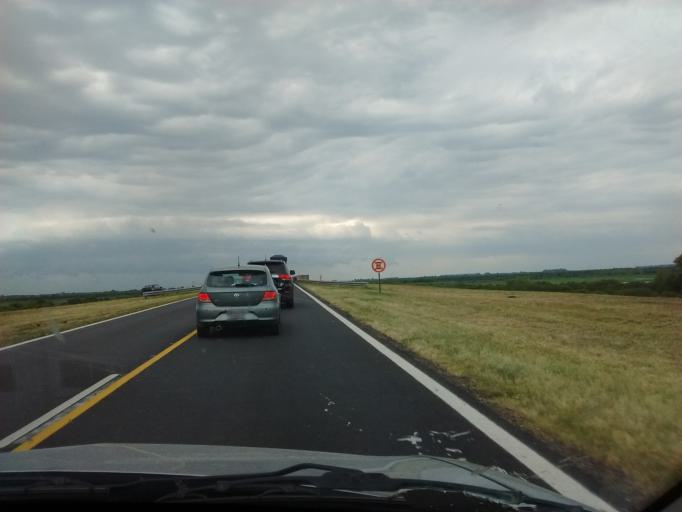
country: AR
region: Santa Fe
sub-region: Departamento de Rosario
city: Rosario
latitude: -32.8630
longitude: -60.6335
